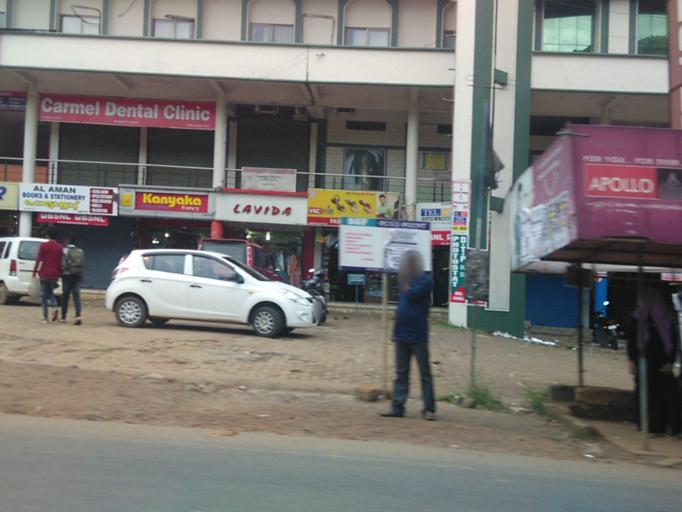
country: IN
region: Kerala
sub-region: Kozhikode
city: Kunnamangalam
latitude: 11.2930
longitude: 75.8253
